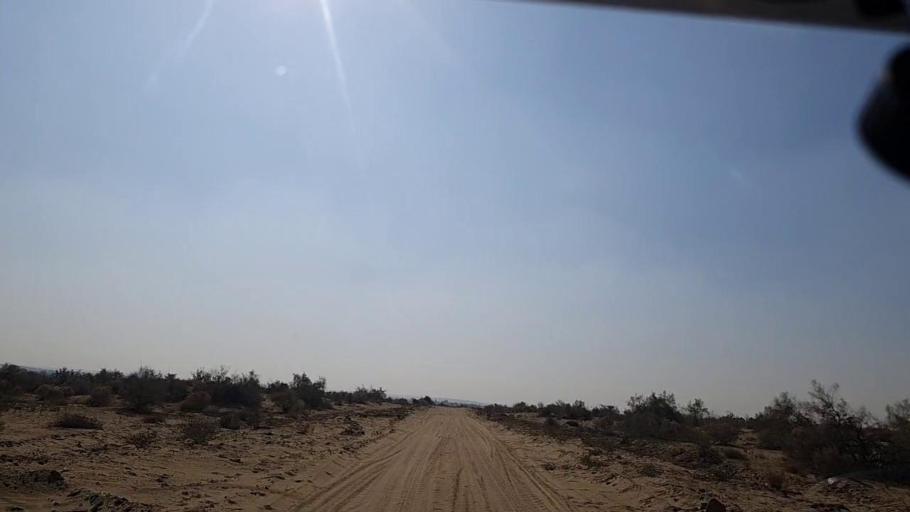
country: PK
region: Sindh
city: Khanpur
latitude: 27.5598
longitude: 69.3883
